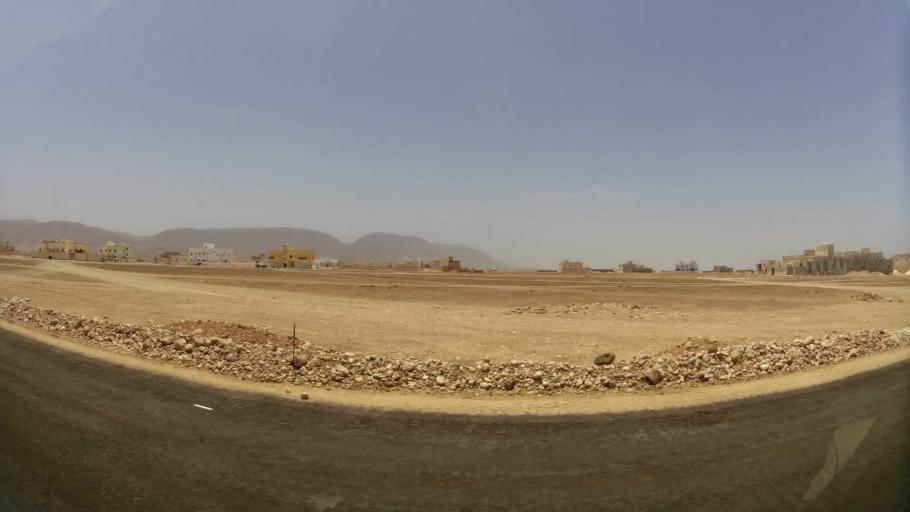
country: OM
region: Zufar
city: Salalah
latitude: 17.0988
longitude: 54.2100
